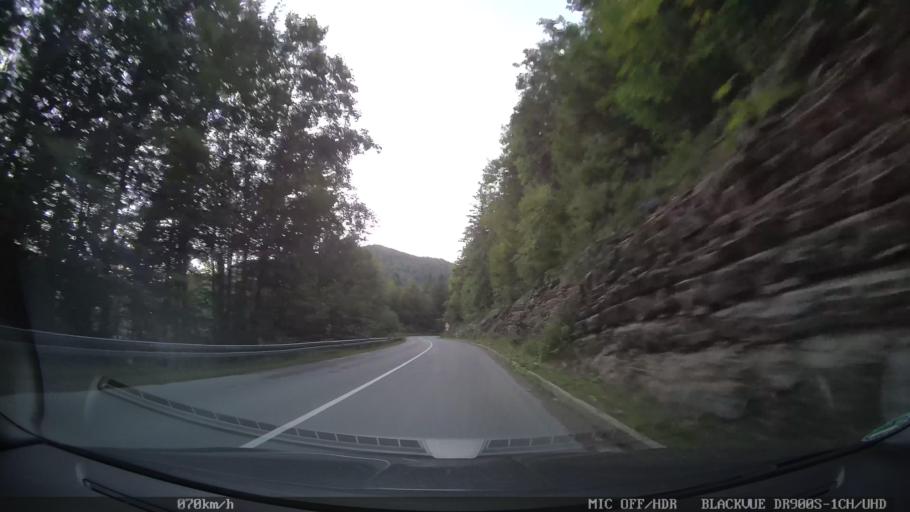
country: HR
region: Primorsko-Goranska
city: Novi Vinodolski
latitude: 45.1635
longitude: 14.9485
